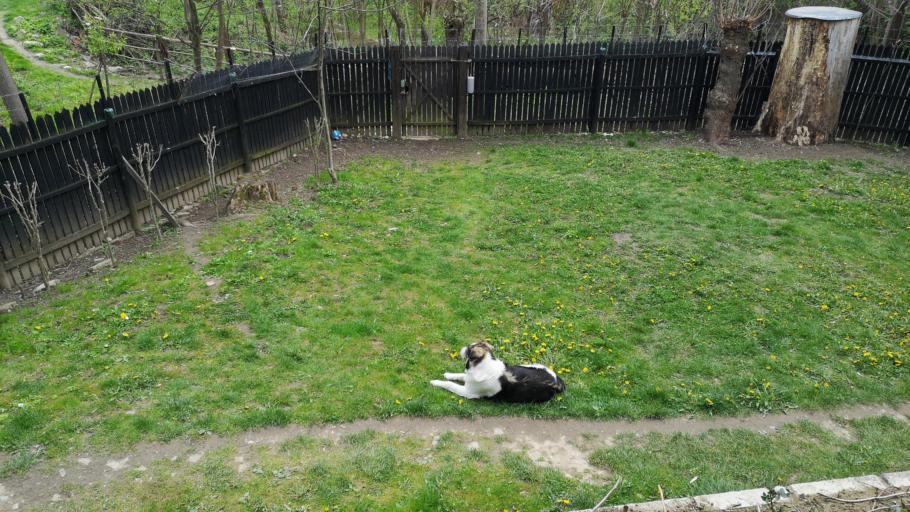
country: RO
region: Prahova
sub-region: Comuna Soimari
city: Soimari
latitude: 45.1843
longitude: 26.2194
